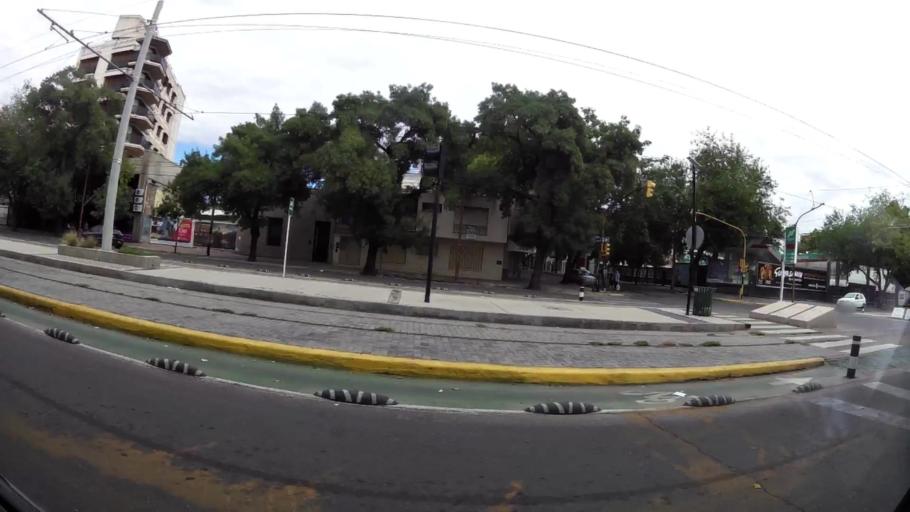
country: AR
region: Mendoza
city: Mendoza
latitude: -32.8867
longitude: -68.8491
